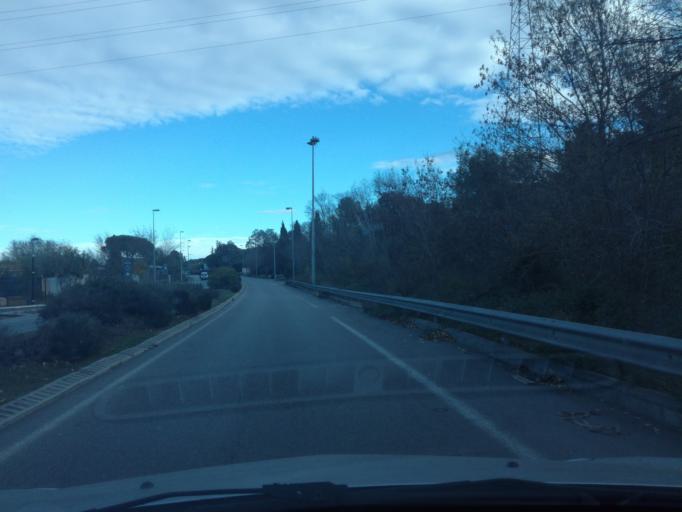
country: FR
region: Provence-Alpes-Cote d'Azur
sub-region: Departement des Alpes-Maritimes
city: Mougins
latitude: 43.6021
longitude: 7.0083
